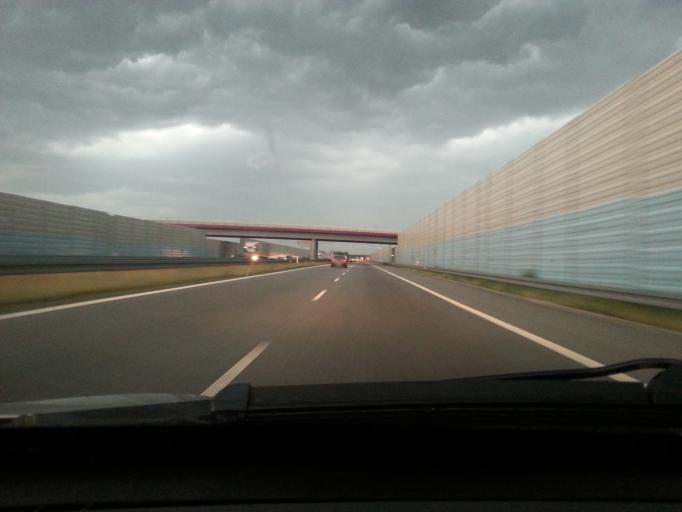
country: PL
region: Lodz Voivodeship
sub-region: powiat Lowicki
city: Lyszkowice
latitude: 51.9779
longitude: 19.8796
